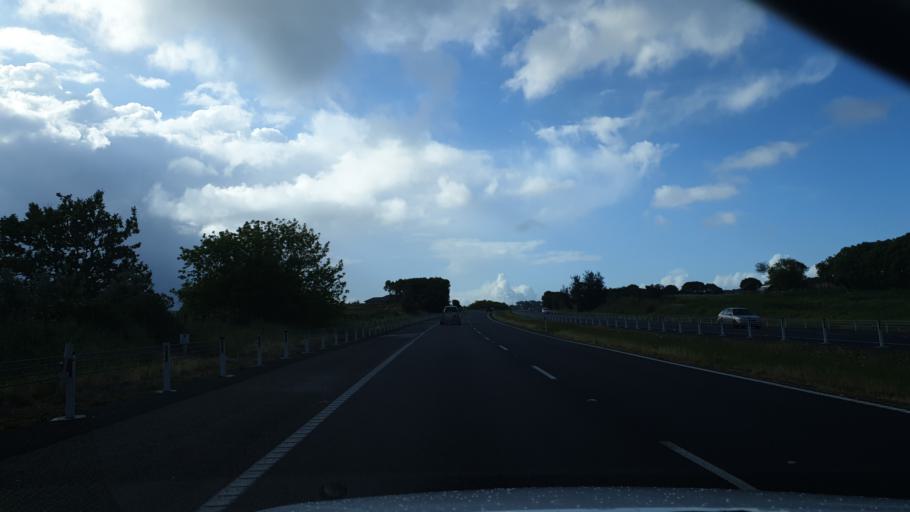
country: NZ
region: Auckland
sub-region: Auckland
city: Pukekohe East
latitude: -37.2444
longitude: 175.0259
